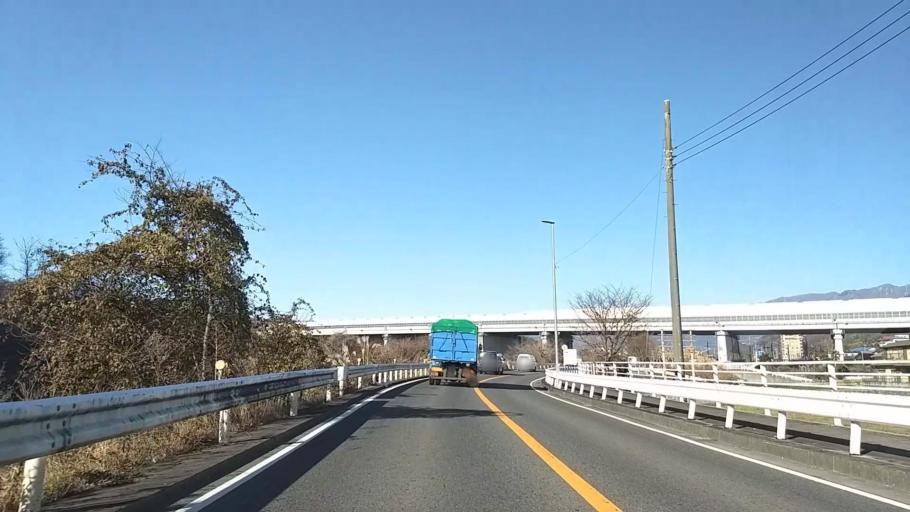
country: JP
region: Kanagawa
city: Hadano
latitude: 35.3584
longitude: 139.2526
